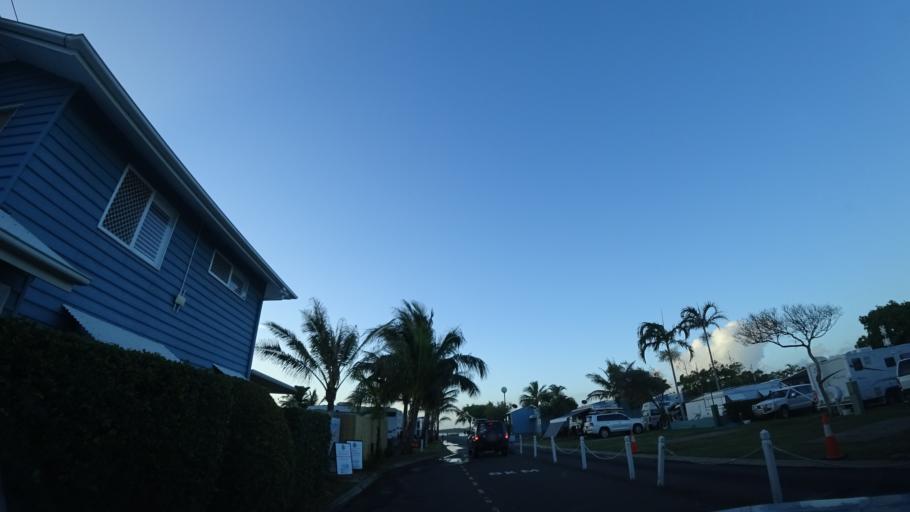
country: AU
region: Queensland
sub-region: Sunshine Coast
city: Mooloolaba
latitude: -26.6536
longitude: 153.0998
